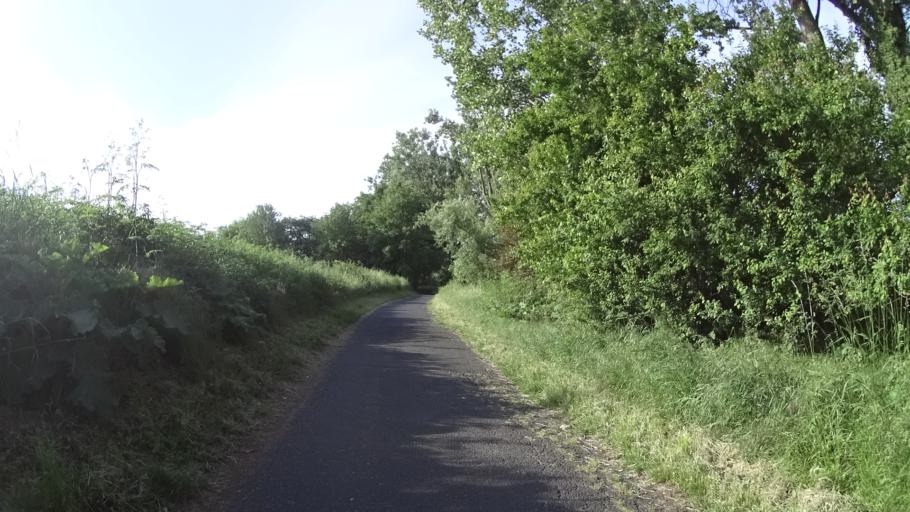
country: DE
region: Hesse
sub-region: Regierungsbezirk Darmstadt
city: Seligenstadt
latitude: 50.0482
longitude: 8.9779
